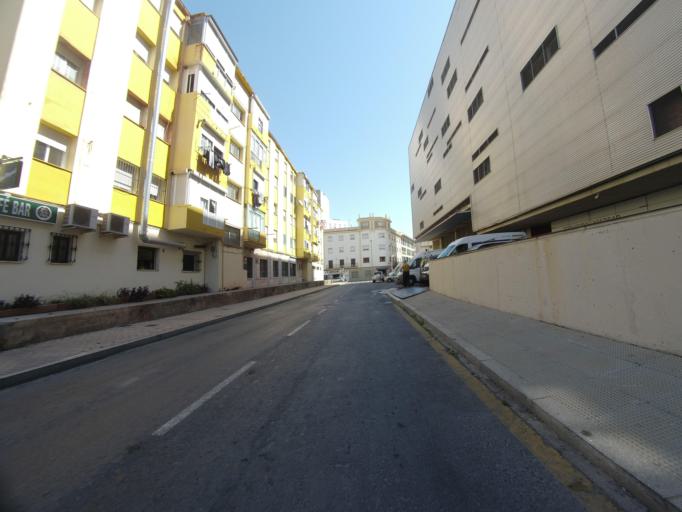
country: ES
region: Andalusia
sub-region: Provincia de Huelva
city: Huelva
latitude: 37.2549
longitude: -6.9563
